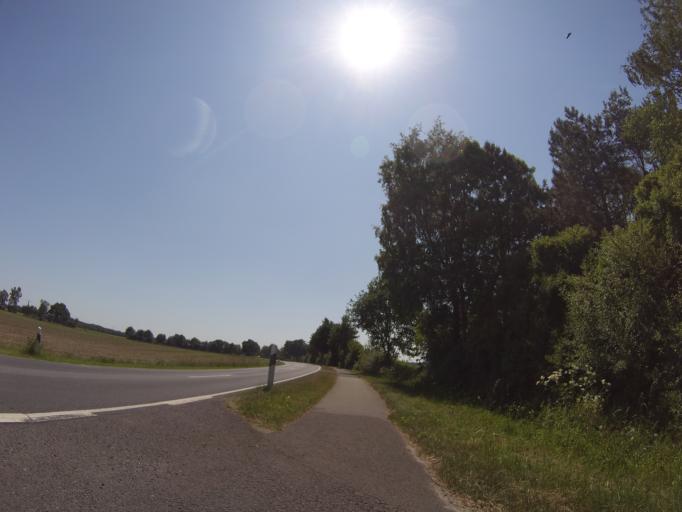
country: DE
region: Lower Saxony
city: Emlichheim
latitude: 52.6384
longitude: 6.8637
